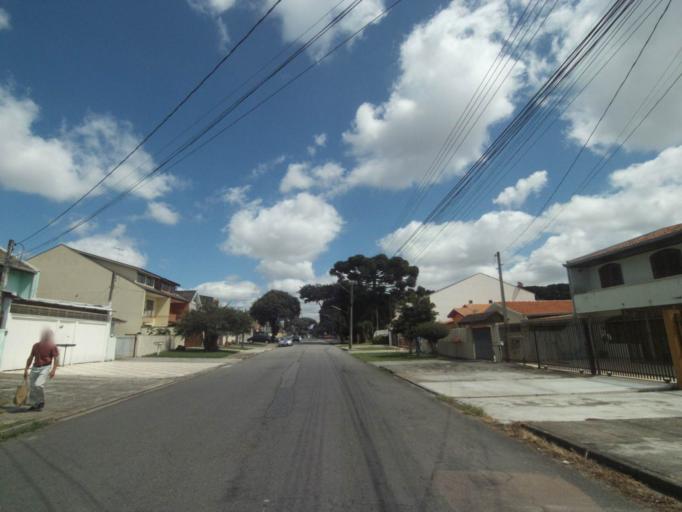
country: BR
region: Parana
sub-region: Pinhais
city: Pinhais
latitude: -25.4380
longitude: -49.2177
